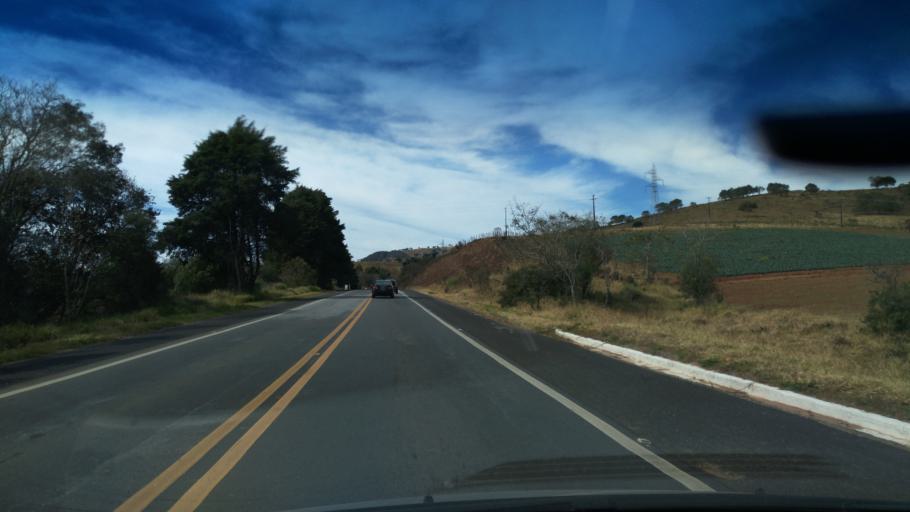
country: BR
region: Minas Gerais
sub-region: Borda Da Mata
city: Borda da Mata
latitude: -22.0713
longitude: -46.2674
